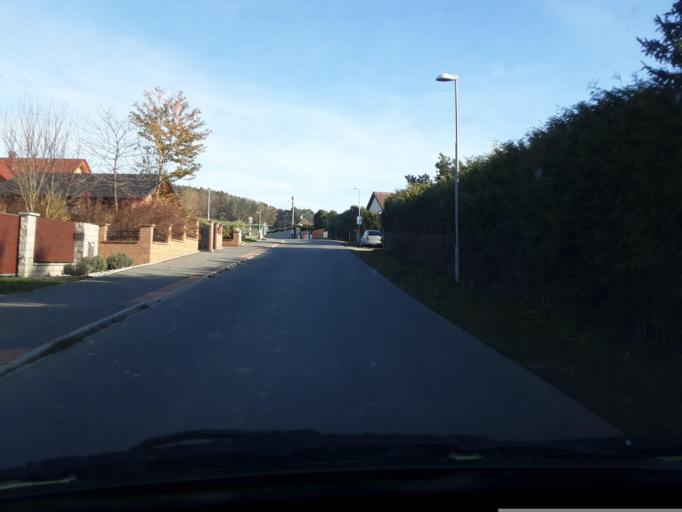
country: CZ
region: Plzensky
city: Klatovy
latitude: 49.3723
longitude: 13.3156
